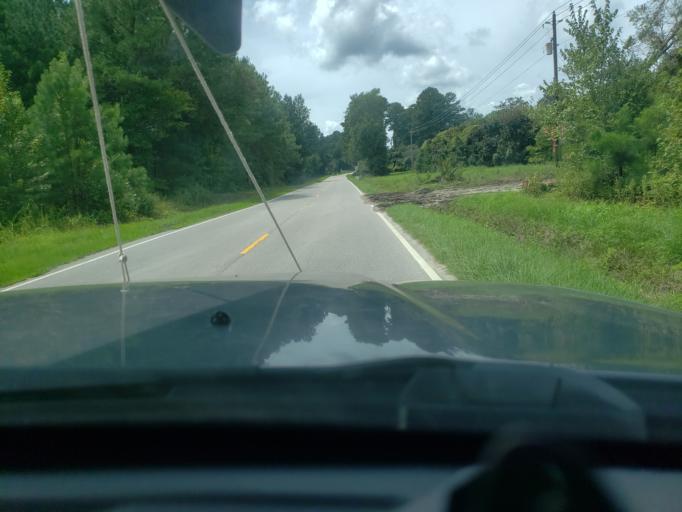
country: US
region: North Carolina
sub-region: Wake County
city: Rolesville
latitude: 35.8821
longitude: -78.3834
